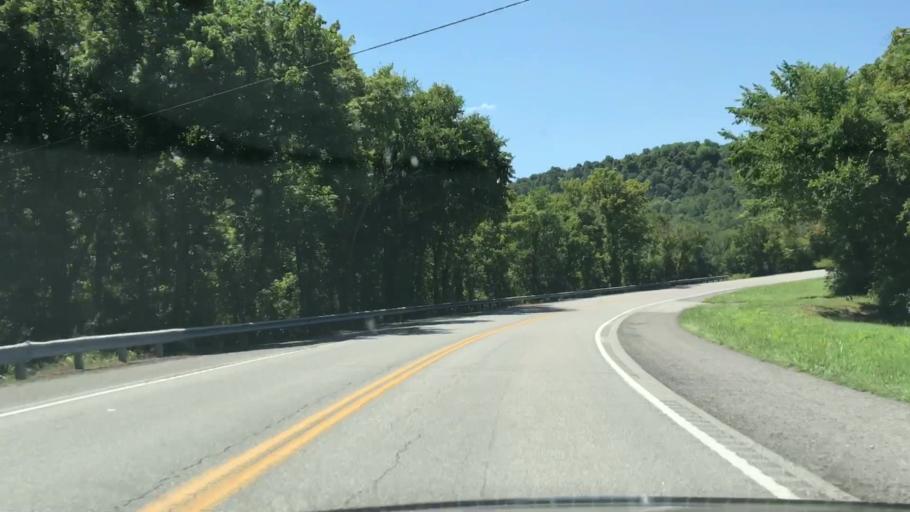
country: US
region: Tennessee
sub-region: Clay County
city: Celina
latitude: 36.4956
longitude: -85.5497
